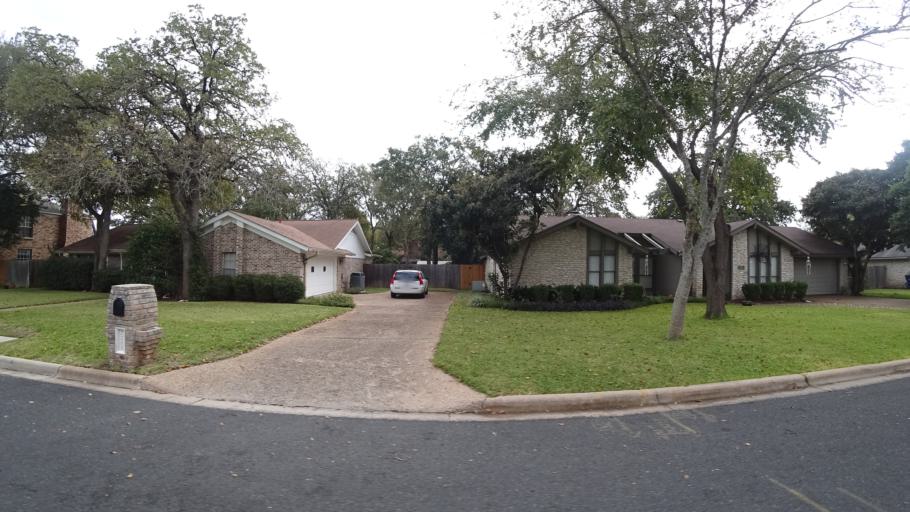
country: US
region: Texas
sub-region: Travis County
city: Shady Hollow
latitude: 30.2140
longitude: -97.8378
